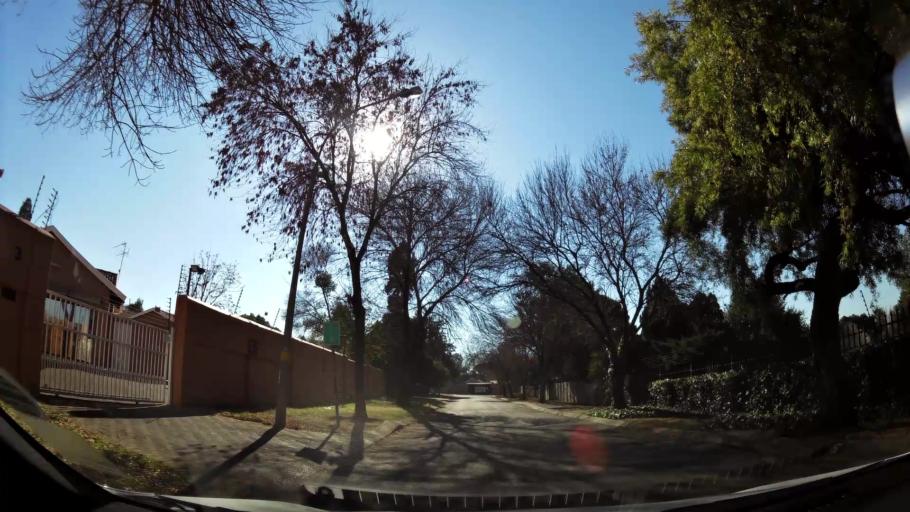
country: ZA
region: Gauteng
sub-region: Ekurhuleni Metropolitan Municipality
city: Germiston
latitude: -26.3360
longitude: 28.1034
